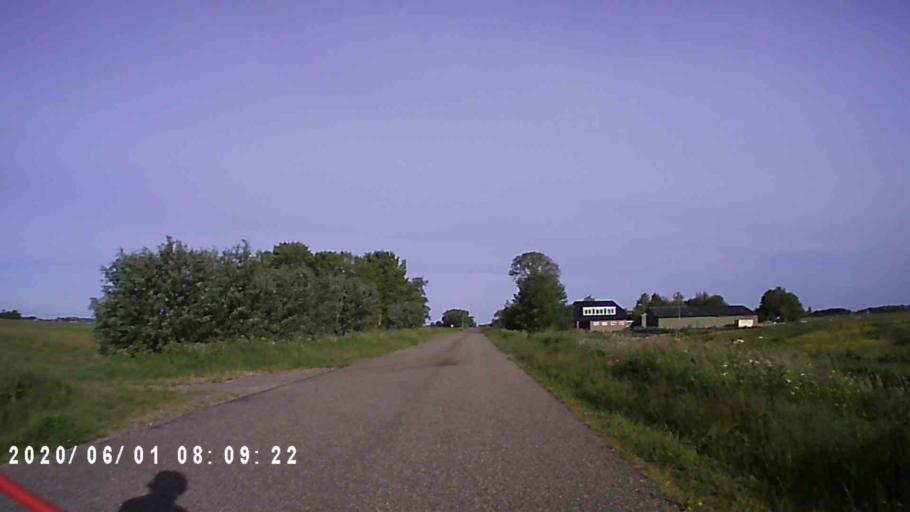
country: NL
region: Friesland
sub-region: Gemeente Ferwerderadiel
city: Burdaard
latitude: 53.2850
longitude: 5.8940
